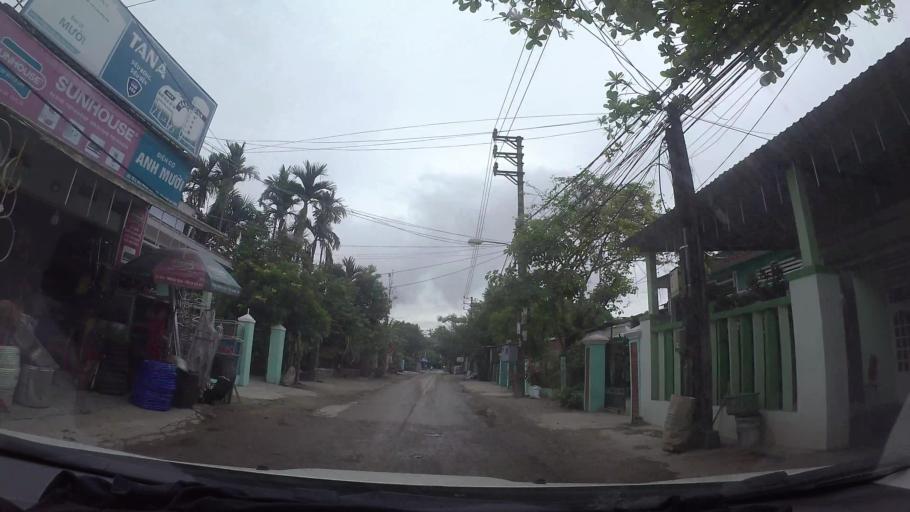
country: VN
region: Da Nang
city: Lien Chieu
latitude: 16.0777
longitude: 108.0988
